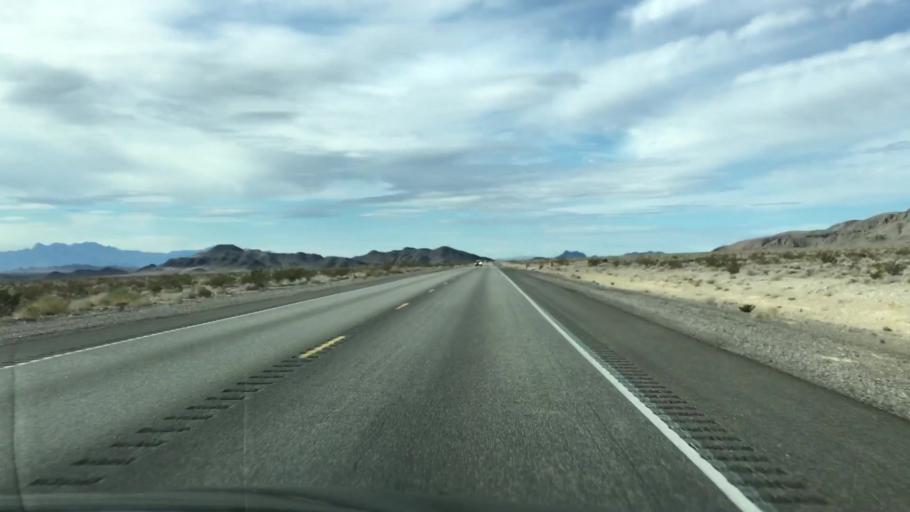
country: US
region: Nevada
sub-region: Nye County
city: Pahrump
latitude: 36.5715
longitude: -116.1706
